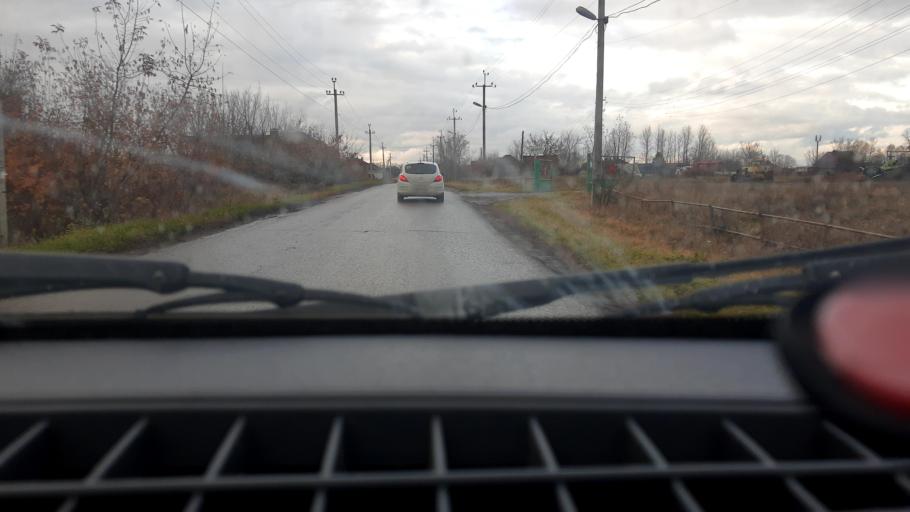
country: RU
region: Bashkortostan
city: Mikhaylovka
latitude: 54.7974
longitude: 55.9378
